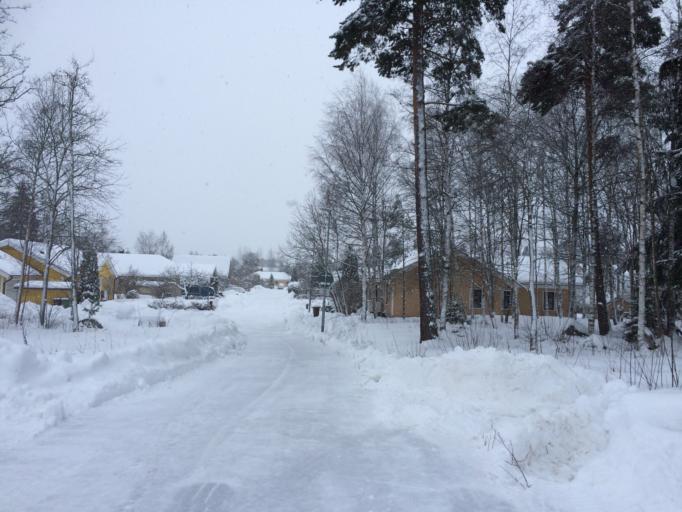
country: SE
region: Vaestmanland
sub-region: Hallstahammars Kommun
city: Hallstahammar
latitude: 59.6282
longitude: 16.2362
